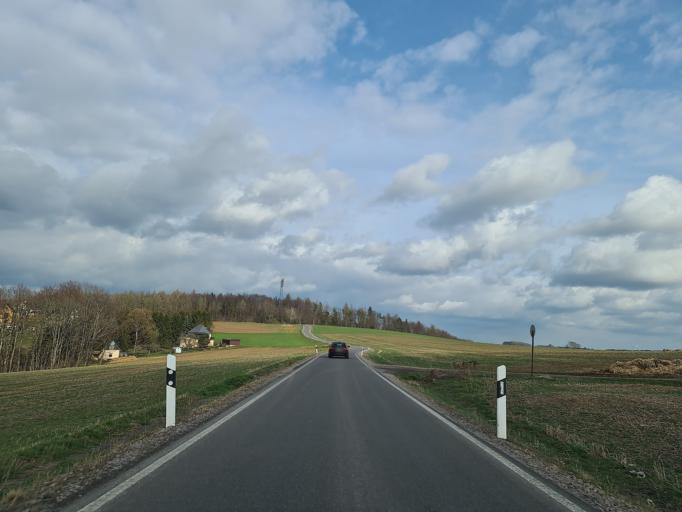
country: DE
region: Saxony
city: Lichtenstein
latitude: 50.7160
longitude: 12.6317
